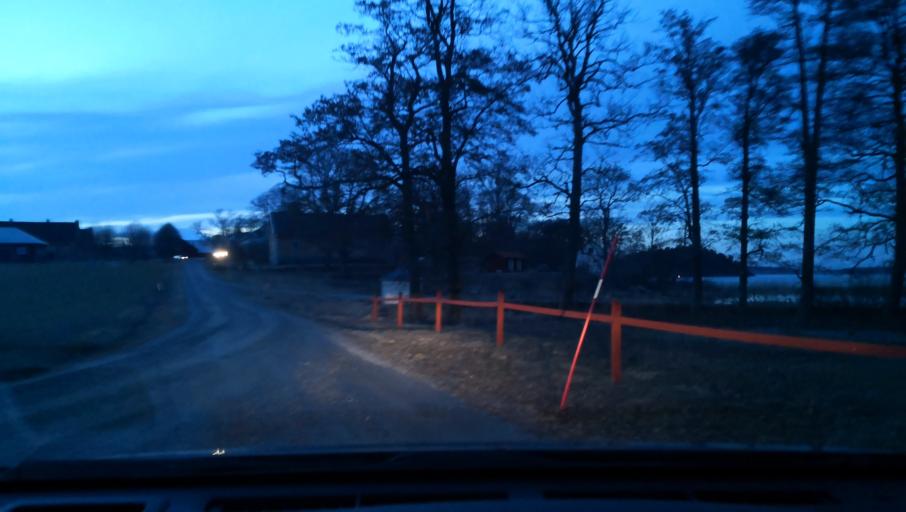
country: SE
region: Uppsala
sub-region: Enkopings Kommun
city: Dalby
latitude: 59.5734
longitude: 17.3798
